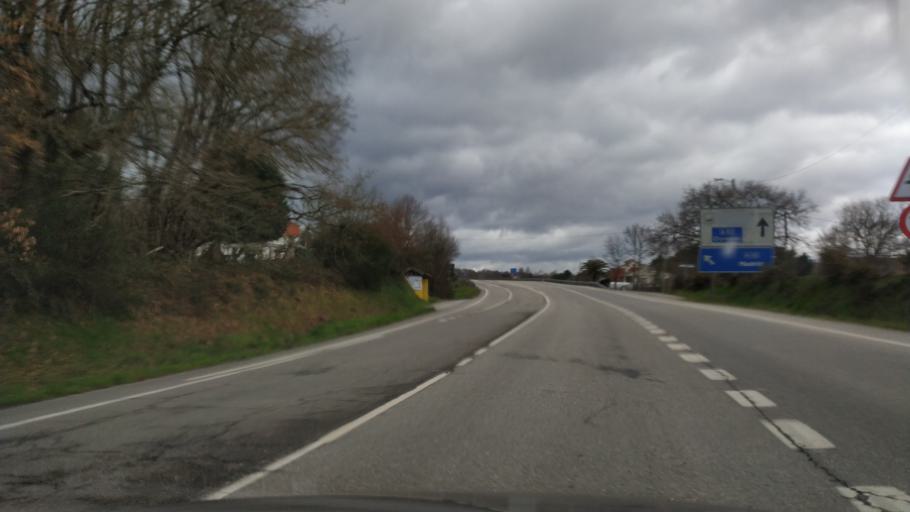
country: ES
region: Galicia
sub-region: Provincia de Ourense
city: Allariz
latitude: 42.2059
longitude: -7.8147
